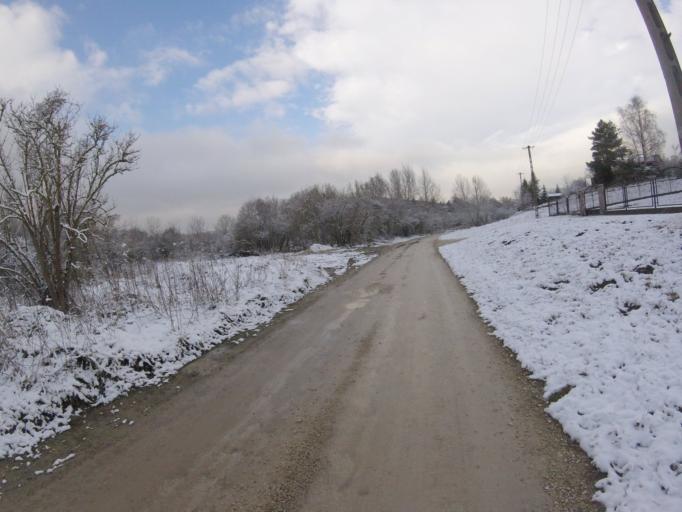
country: HU
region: Komarom-Esztergom
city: Esztergom
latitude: 47.7925
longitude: 18.7999
